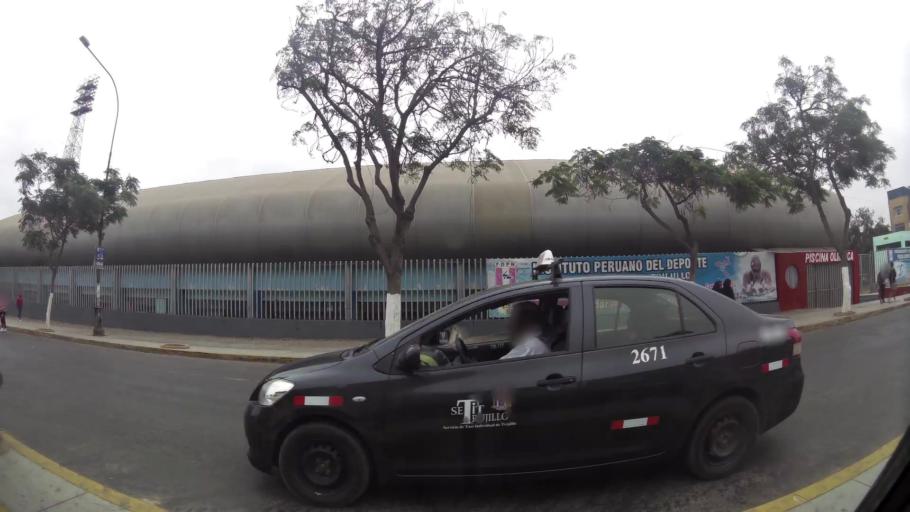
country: PE
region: La Libertad
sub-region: Provincia de Trujillo
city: Trujillo
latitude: -8.1066
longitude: -79.0294
